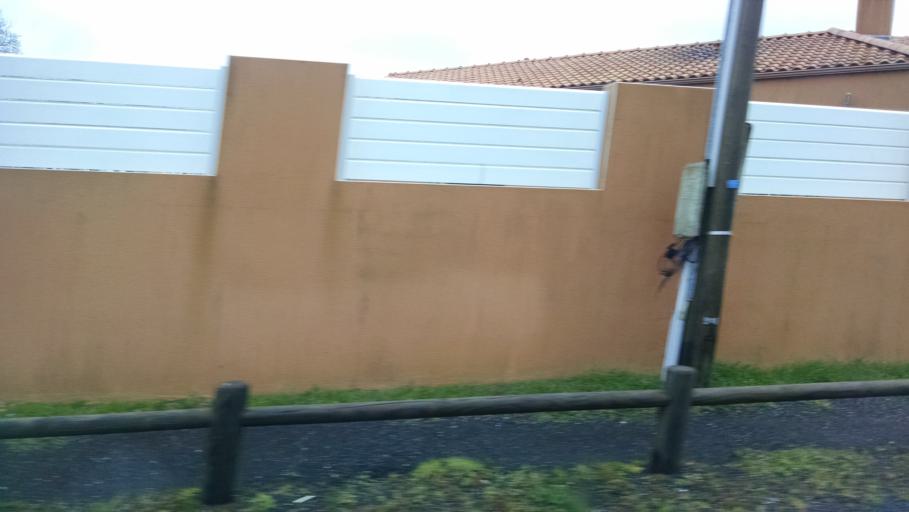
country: FR
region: Pays de la Loire
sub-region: Departement de la Loire-Atlantique
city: Aigrefeuille-sur-Maine
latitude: 47.0838
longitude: -1.4054
